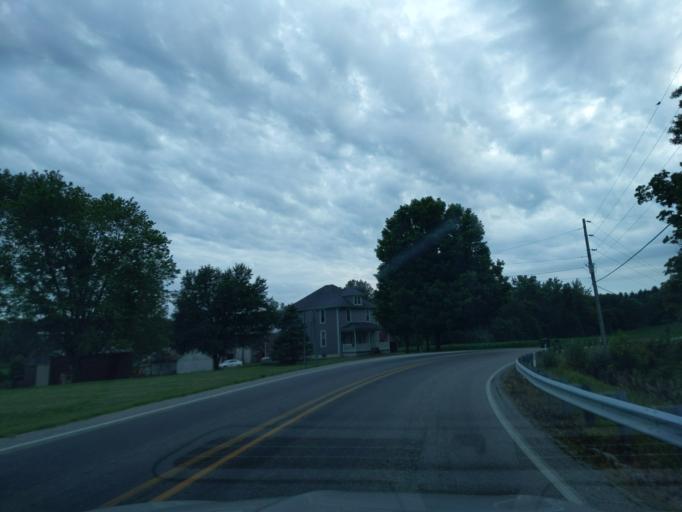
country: US
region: Indiana
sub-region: Ripley County
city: Osgood
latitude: 39.1952
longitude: -85.2534
